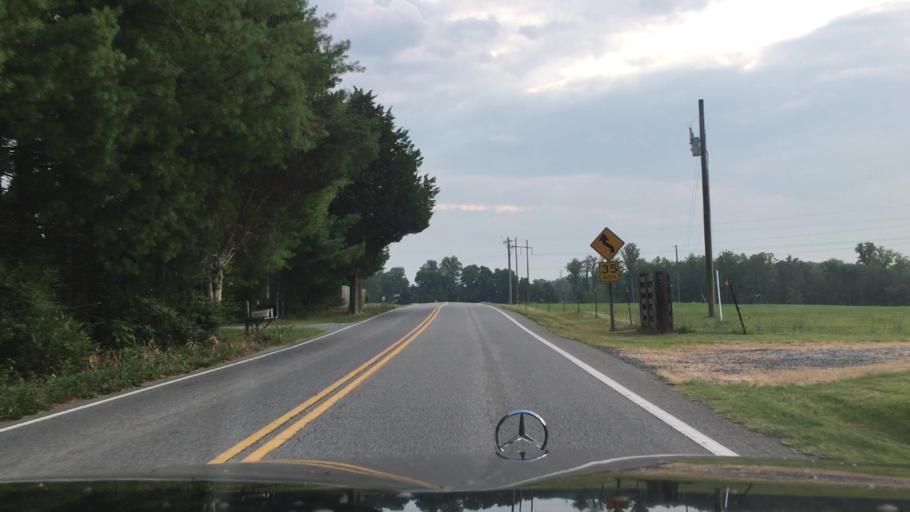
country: US
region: Virginia
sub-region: Campbell County
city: Timberlake
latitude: 37.2866
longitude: -79.3188
